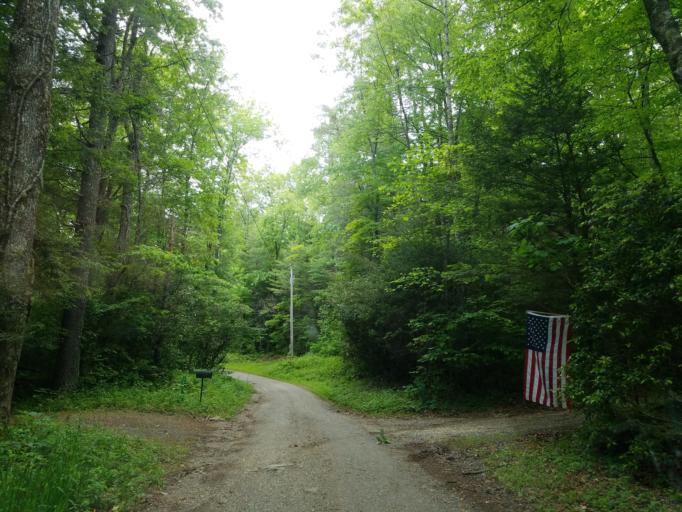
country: US
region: Georgia
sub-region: Union County
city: Blairsville
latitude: 34.7308
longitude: -83.9691
